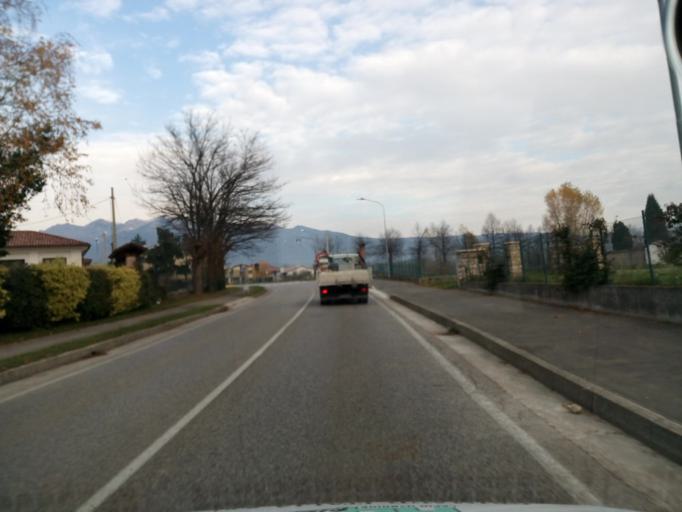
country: IT
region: Veneto
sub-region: Provincia di Treviso
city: Castelcucco
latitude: 45.8085
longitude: 11.8896
